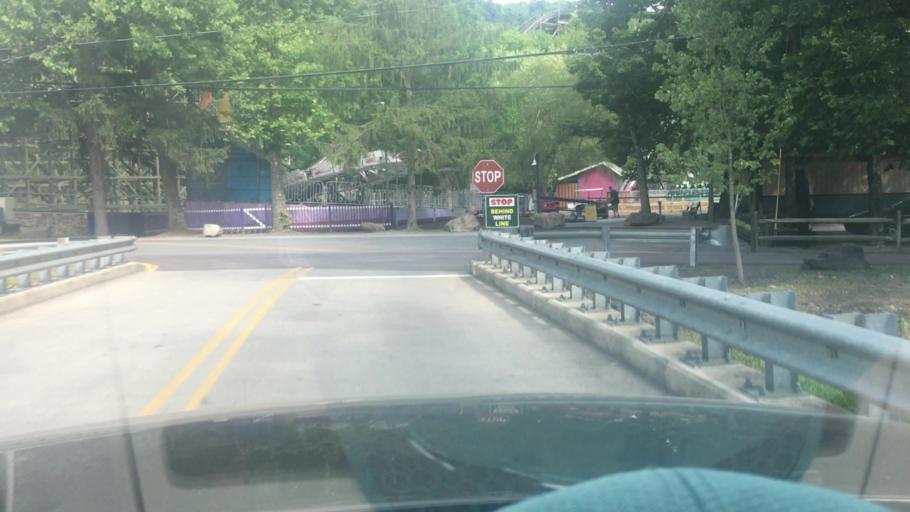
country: US
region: Pennsylvania
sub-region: Northumberland County
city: Elysburg
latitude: 40.8769
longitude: -76.5059
